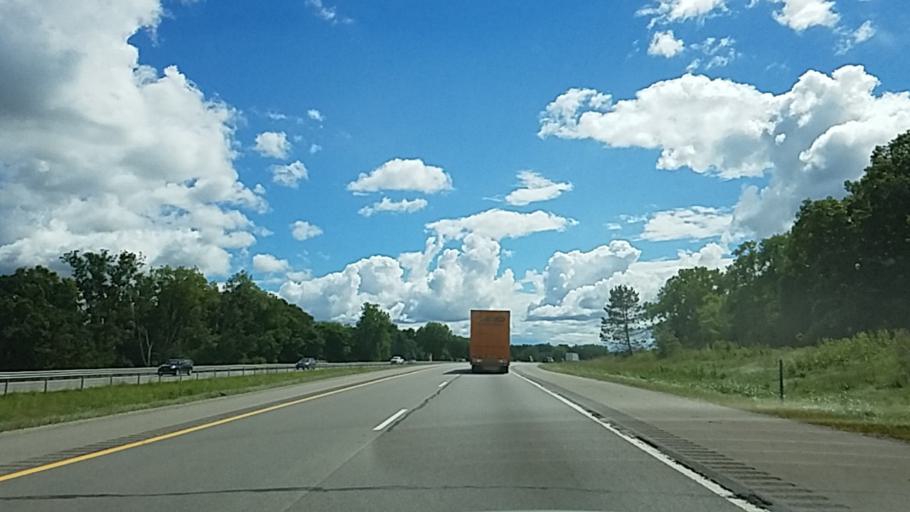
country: US
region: Michigan
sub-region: Livingston County
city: Whitmore Lake
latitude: 42.4796
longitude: -83.7559
